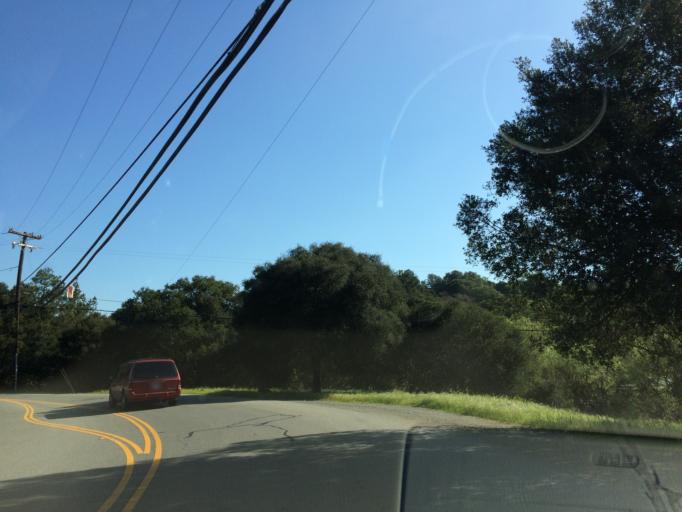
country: US
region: California
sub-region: Santa Clara County
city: Los Altos Hills
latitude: 37.3767
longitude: -122.1625
